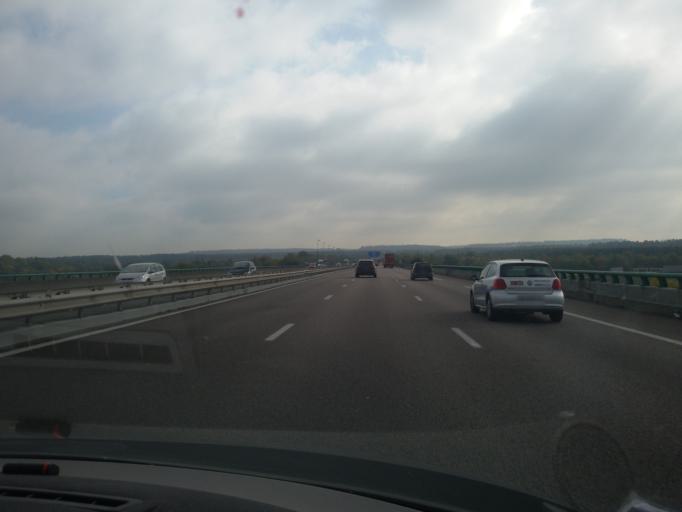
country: FR
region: Haute-Normandie
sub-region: Departement de l'Eure
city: Criquebeuf-sur-Seine
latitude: 49.3079
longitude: 1.1140
